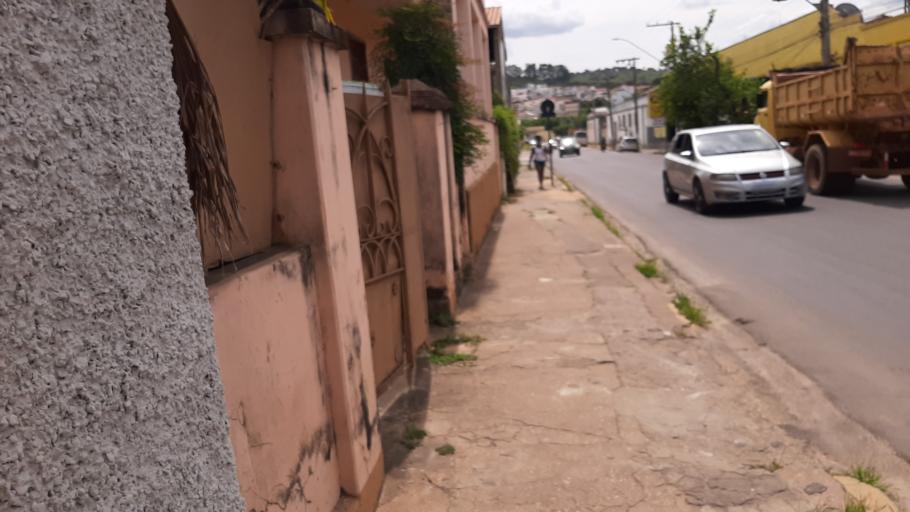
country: BR
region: Minas Gerais
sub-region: Lavras
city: Lavras
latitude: -21.2276
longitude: -45.0022
